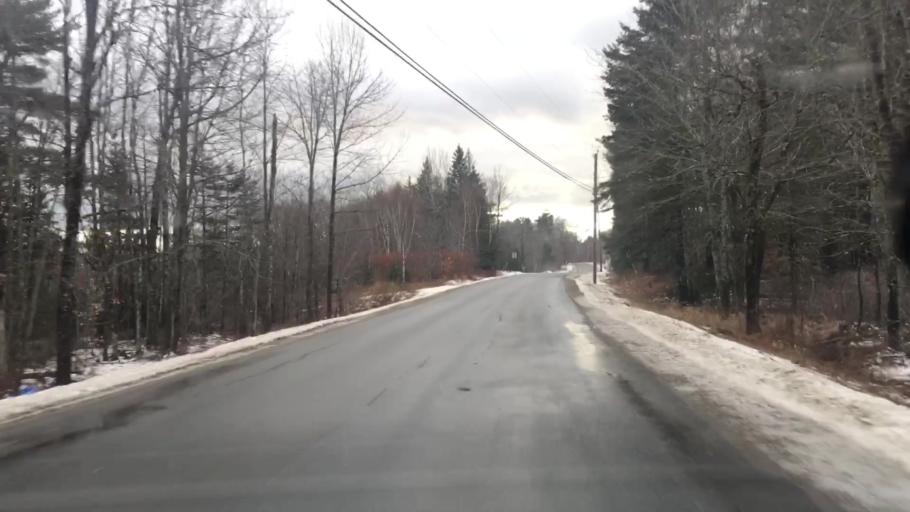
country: US
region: Maine
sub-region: Hancock County
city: Dedham
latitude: 44.6475
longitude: -68.7051
